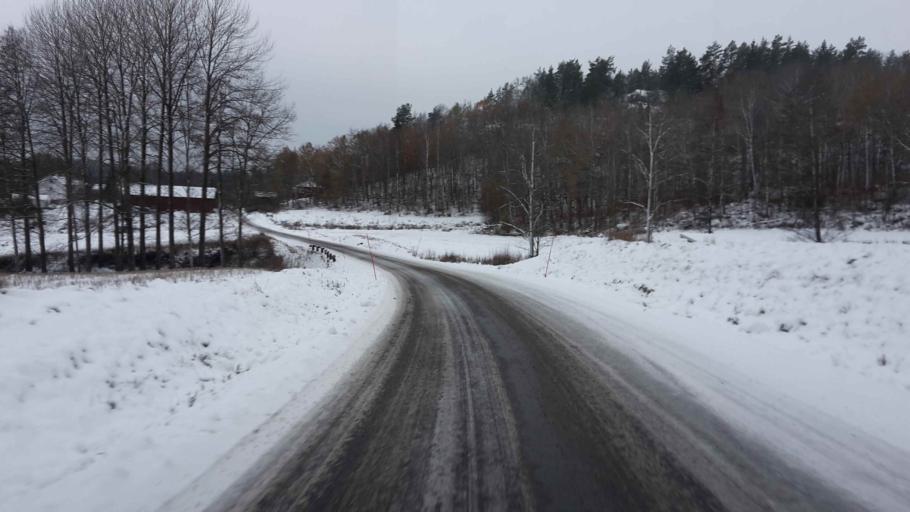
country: SE
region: Kalmar
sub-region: Vasterviks Kommun
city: Overum
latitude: 58.1490
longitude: 16.2197
